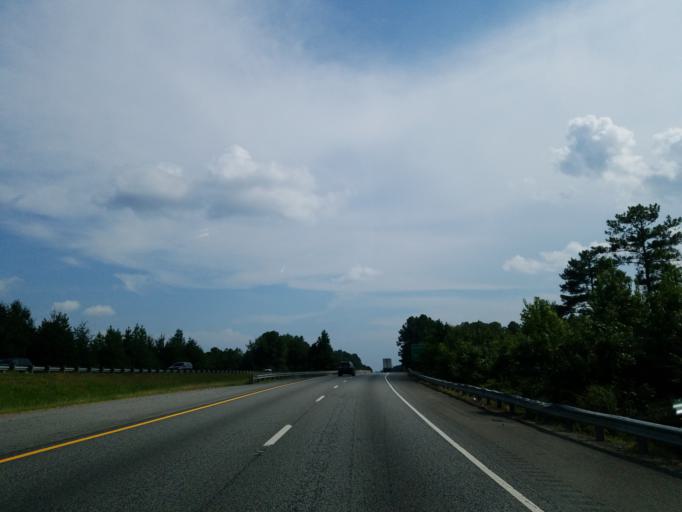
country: US
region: Georgia
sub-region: Monroe County
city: Forsyth
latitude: 32.9557
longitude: -83.8113
